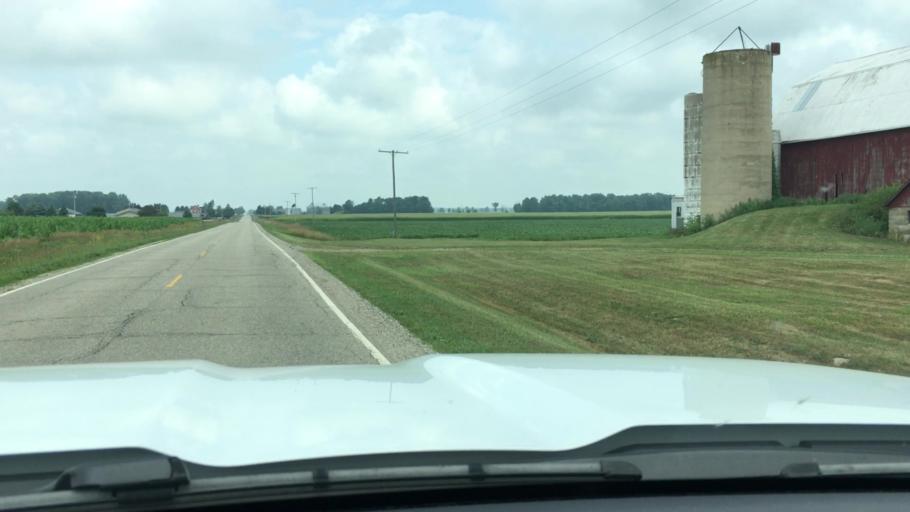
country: US
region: Michigan
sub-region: Sanilac County
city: Marlette
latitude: 43.3594
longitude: -83.0058
